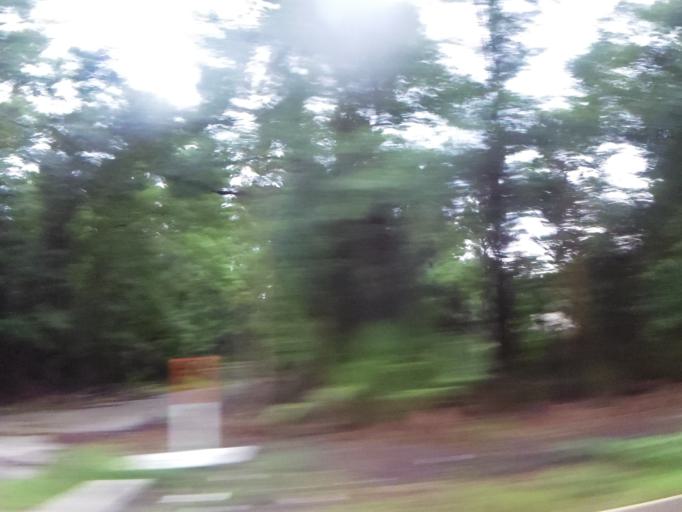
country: US
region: Florida
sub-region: Duval County
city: Jacksonville
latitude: 30.2775
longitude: -81.5643
